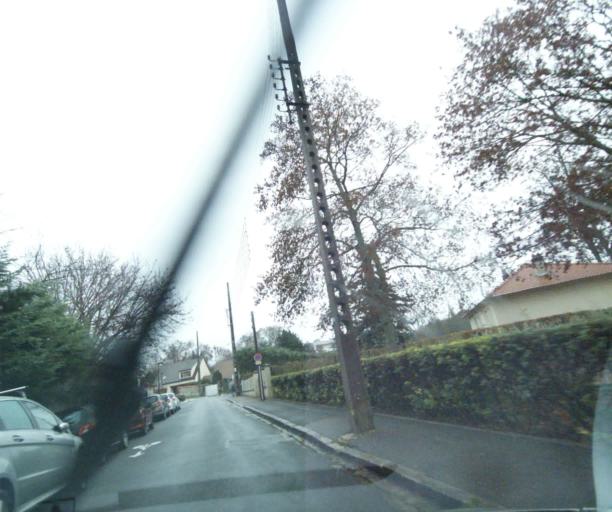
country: FR
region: Ile-de-France
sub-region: Departement de Seine-et-Marne
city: Avon
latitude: 48.4166
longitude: 2.7341
